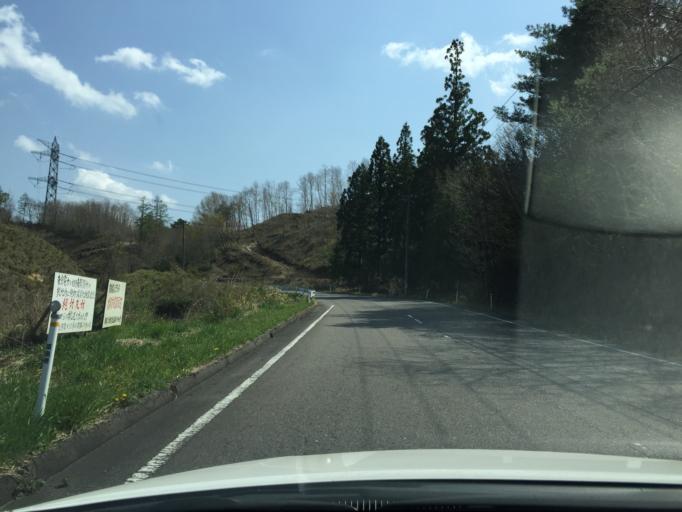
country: JP
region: Fukushima
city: Namie
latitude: 37.3853
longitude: 140.7984
